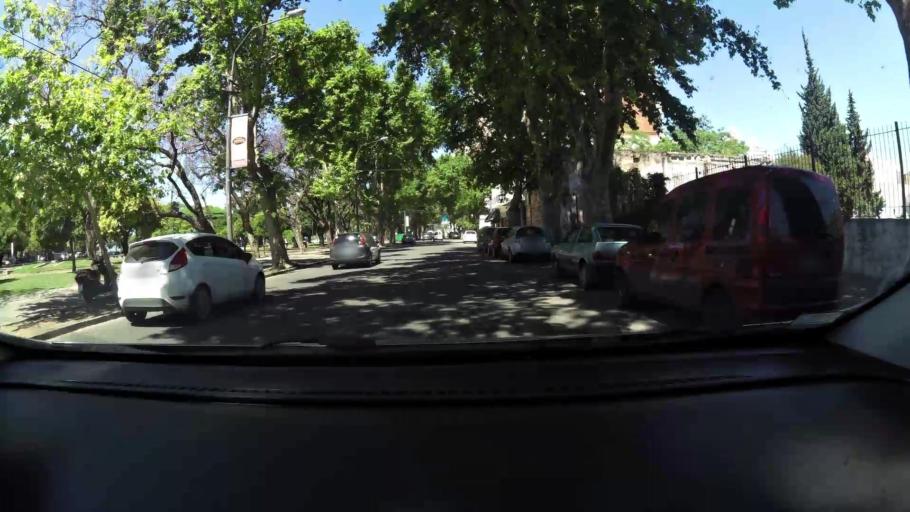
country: AR
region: Santa Fe
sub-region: Departamento de Rosario
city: Rosario
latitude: -32.9317
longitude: -60.6525
